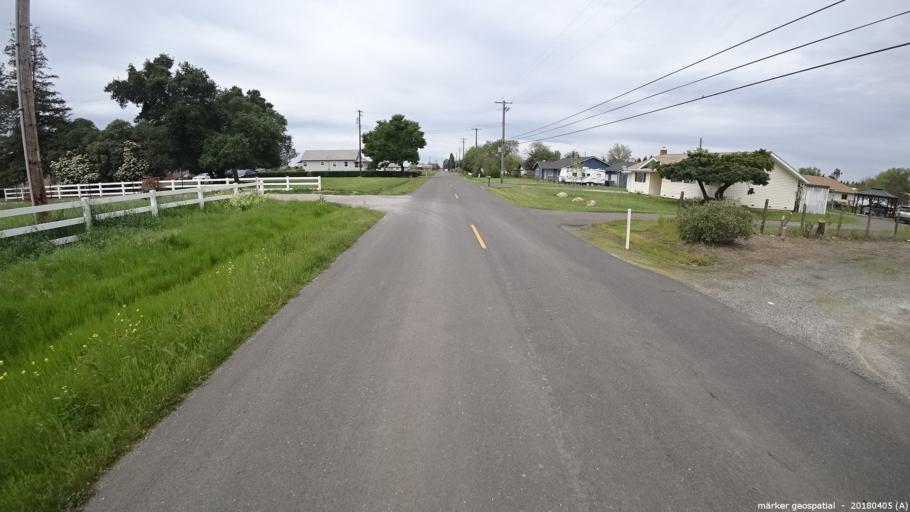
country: US
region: California
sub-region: Sacramento County
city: Galt
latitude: 38.2838
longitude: -121.3111
